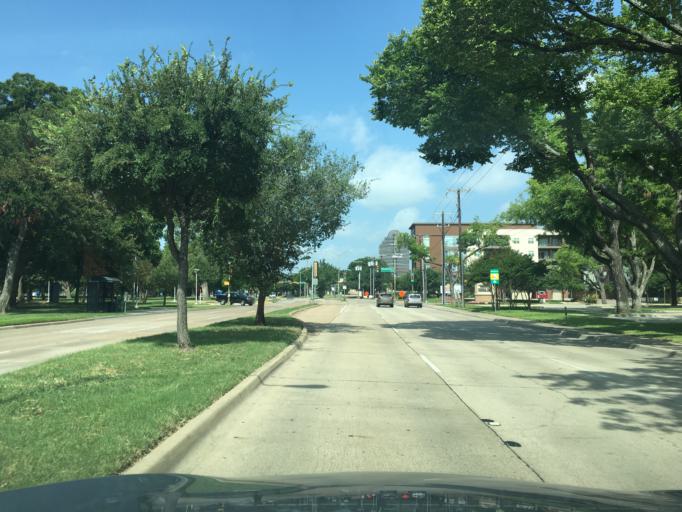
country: US
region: Texas
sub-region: Dallas County
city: University Park
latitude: 32.8834
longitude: -96.7611
